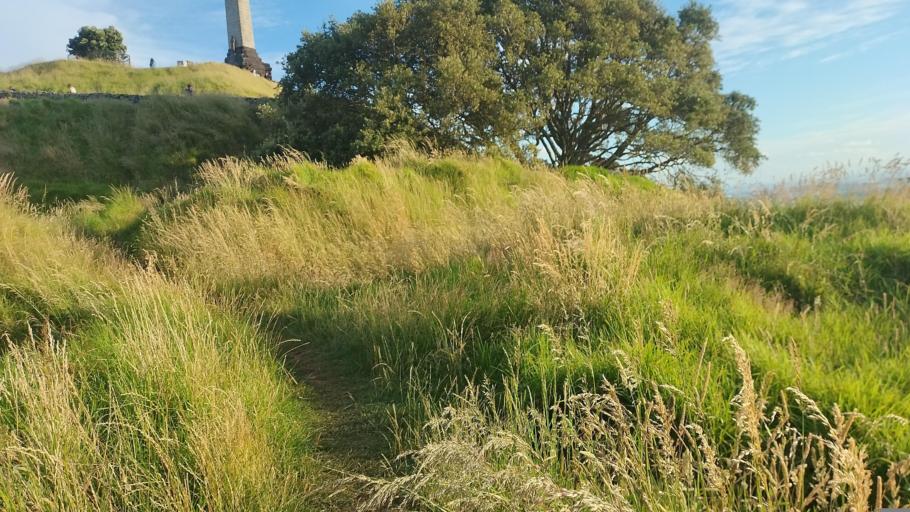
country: NZ
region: Auckland
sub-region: Auckland
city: Auckland
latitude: -36.8994
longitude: 174.7825
